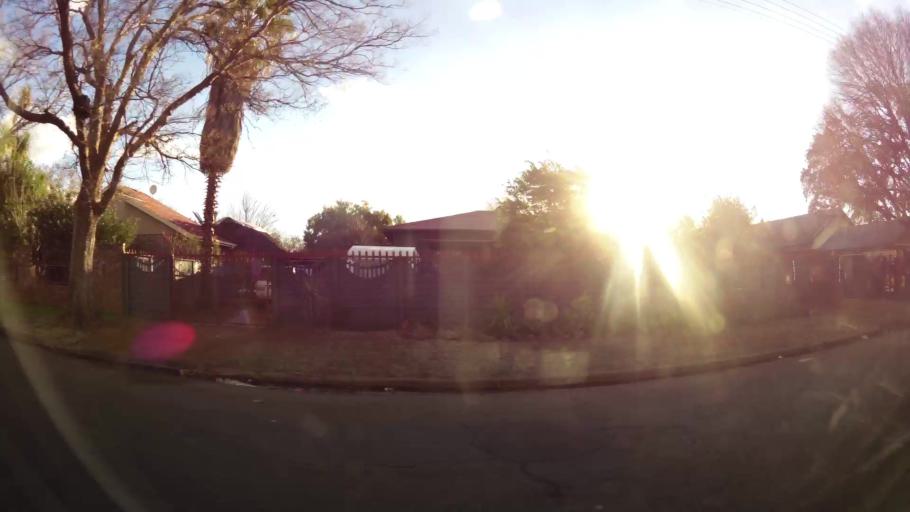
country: ZA
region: North-West
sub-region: Dr Kenneth Kaunda District Municipality
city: Potchefstroom
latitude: -26.7208
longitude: 27.1006
